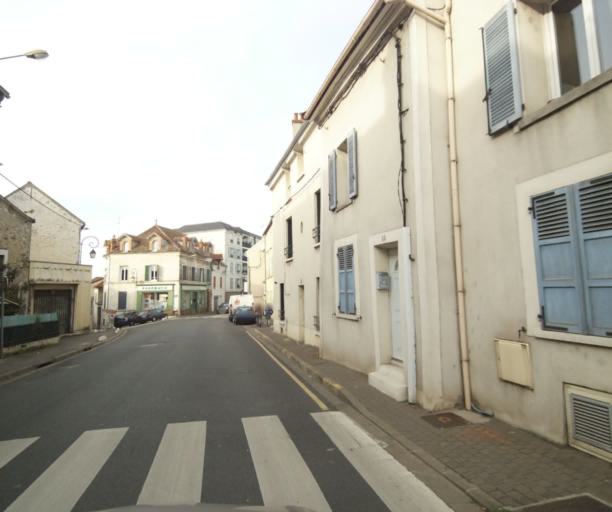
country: FR
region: Ile-de-France
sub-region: Departement des Yvelines
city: Triel-sur-Seine
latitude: 48.9771
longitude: 2.0055
